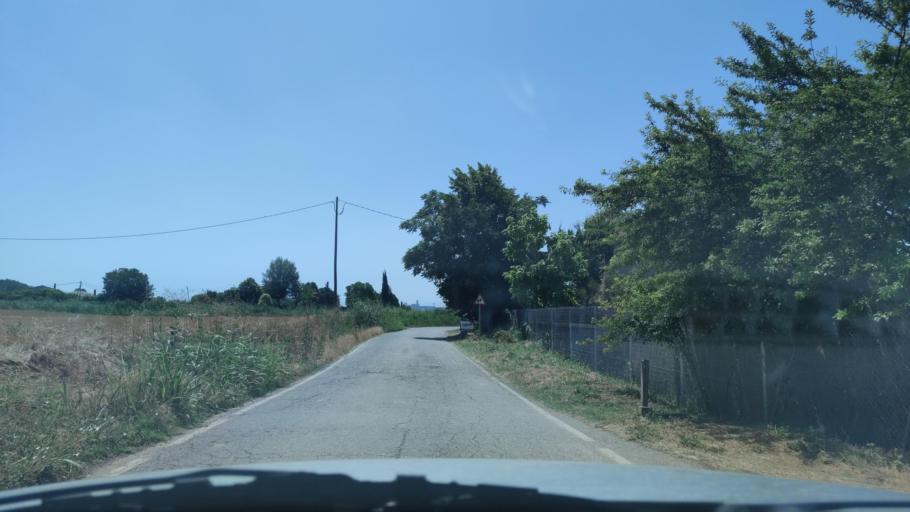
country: ES
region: Catalonia
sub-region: Provincia de Lleida
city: Torrefarrera
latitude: 41.6510
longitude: 0.5984
